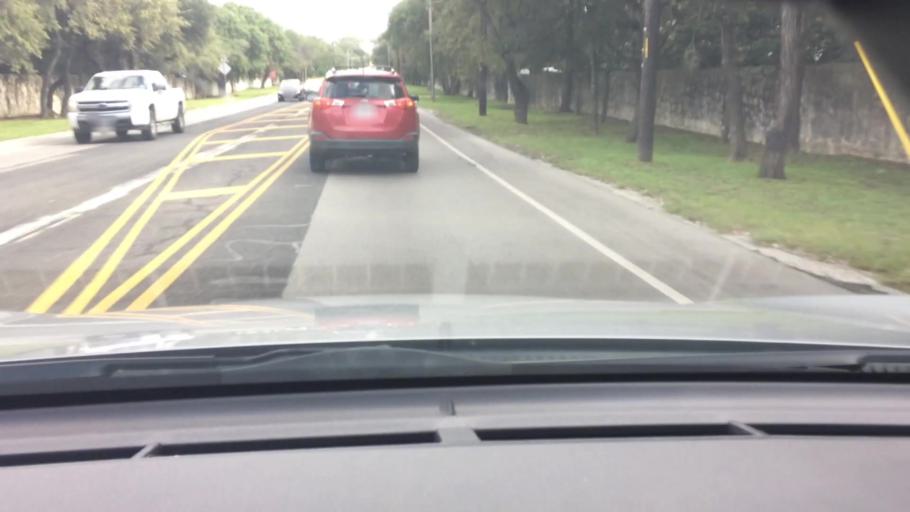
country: US
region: Texas
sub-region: Bexar County
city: Shavano Park
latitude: 29.5589
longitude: -98.5511
